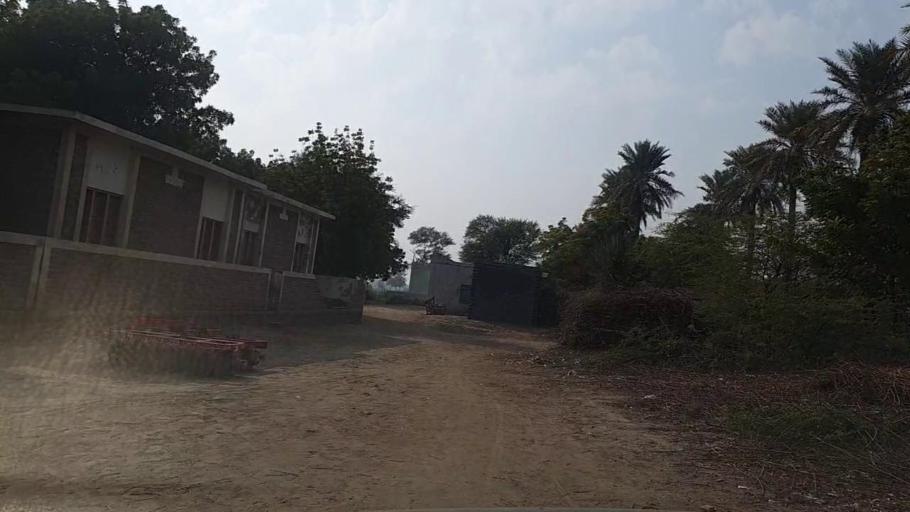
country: PK
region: Sindh
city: Nawabshah
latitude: 26.2825
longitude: 68.4433
